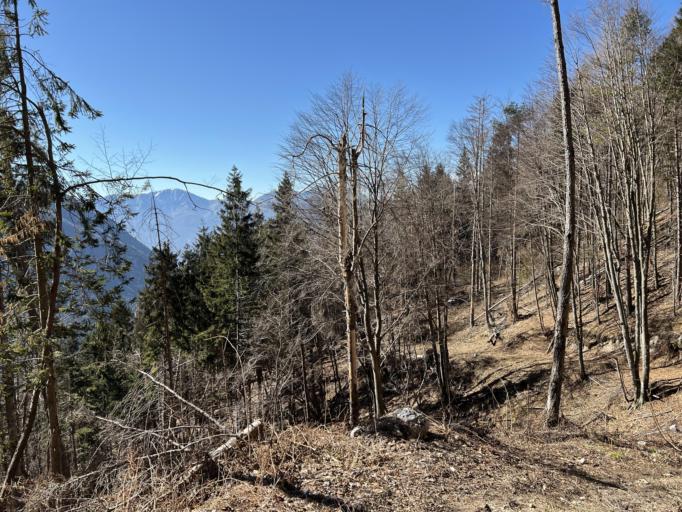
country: IT
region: Friuli Venezia Giulia
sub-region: Provincia di Udine
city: Zuglio
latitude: 46.4445
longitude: 13.0683
